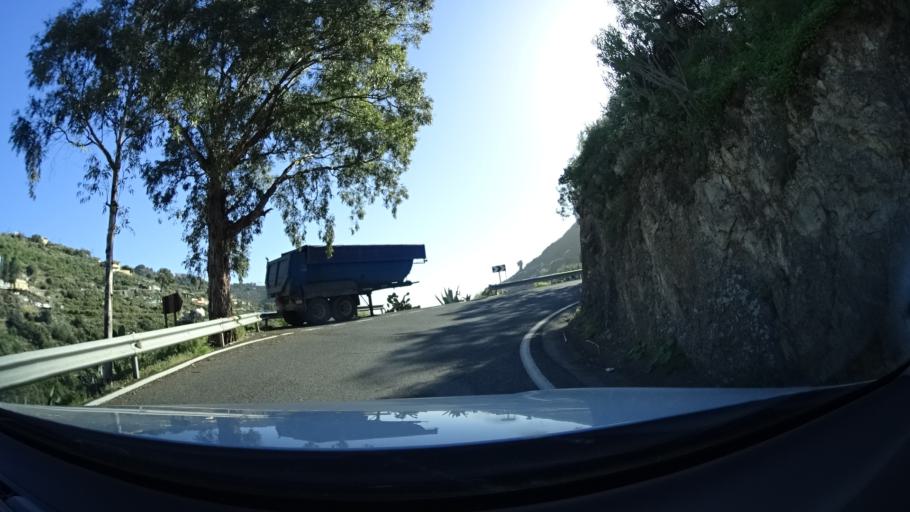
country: ES
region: Canary Islands
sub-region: Provincia de Las Palmas
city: Santa Brigida
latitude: 28.0215
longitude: -15.4750
